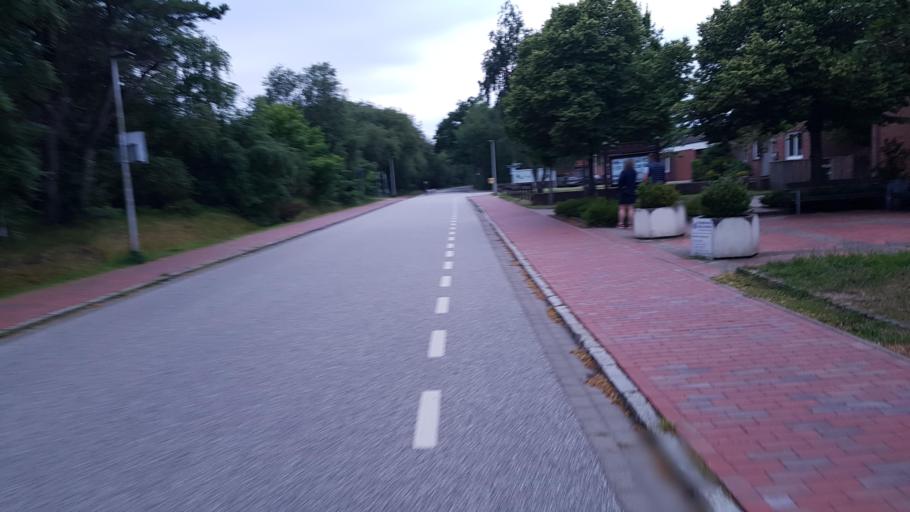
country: DE
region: Schleswig-Holstein
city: Sankt Peter-Ording
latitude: 54.3062
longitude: 8.6273
